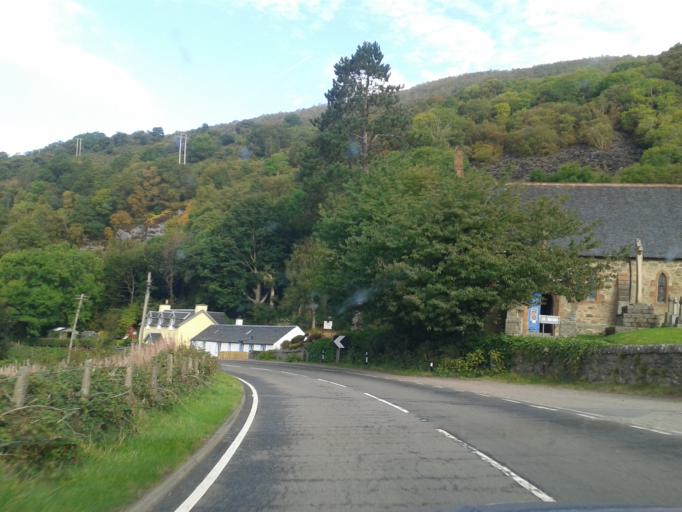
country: GB
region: Scotland
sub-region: Highland
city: Fort William
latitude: 56.6998
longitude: -5.1832
